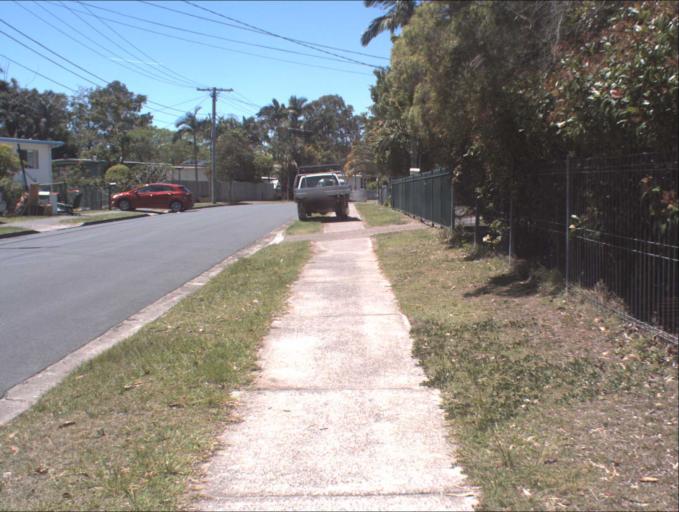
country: AU
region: Queensland
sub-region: Logan
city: Logan City
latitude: -27.6431
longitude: 153.1249
